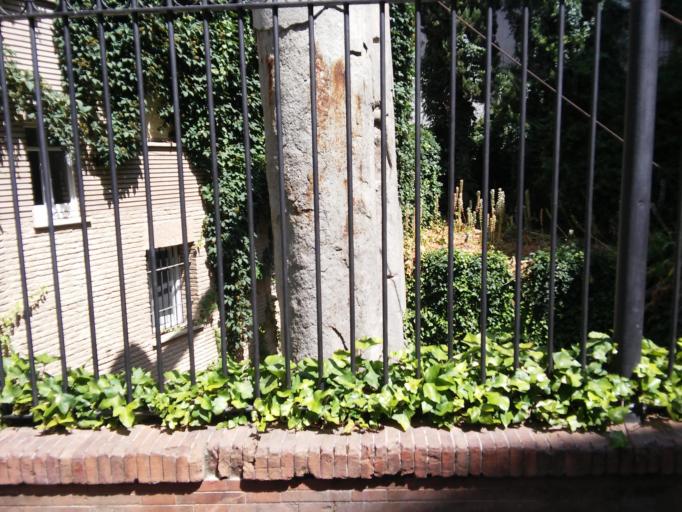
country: ES
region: Andalusia
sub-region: Provincia de Sevilla
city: Sevilla
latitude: 37.3880
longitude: -5.9904
